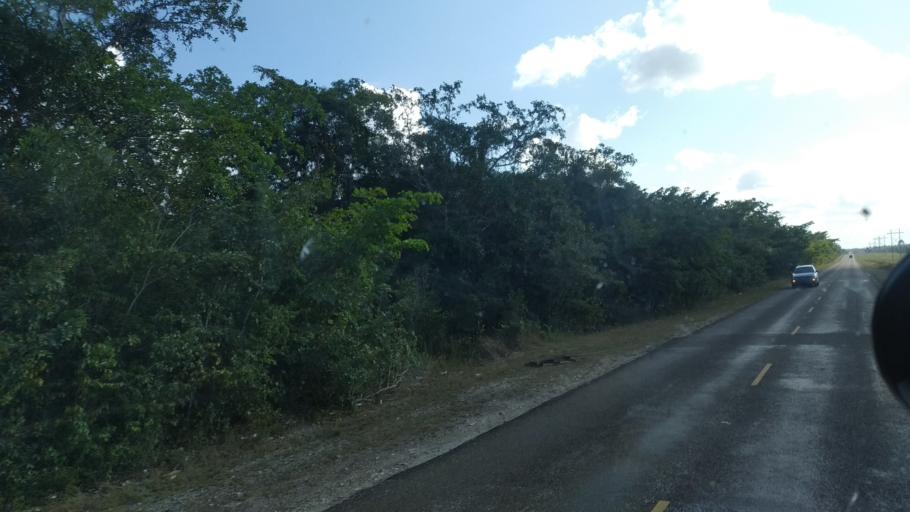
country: BZ
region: Cayo
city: Belmopan
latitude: 17.3736
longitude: -88.5300
